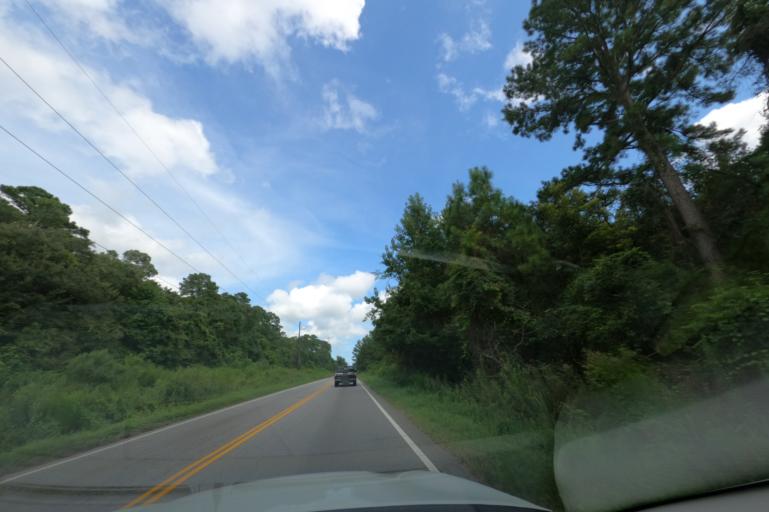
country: US
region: South Carolina
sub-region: Charleston County
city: Shell Point
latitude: 32.7226
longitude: -80.0893
